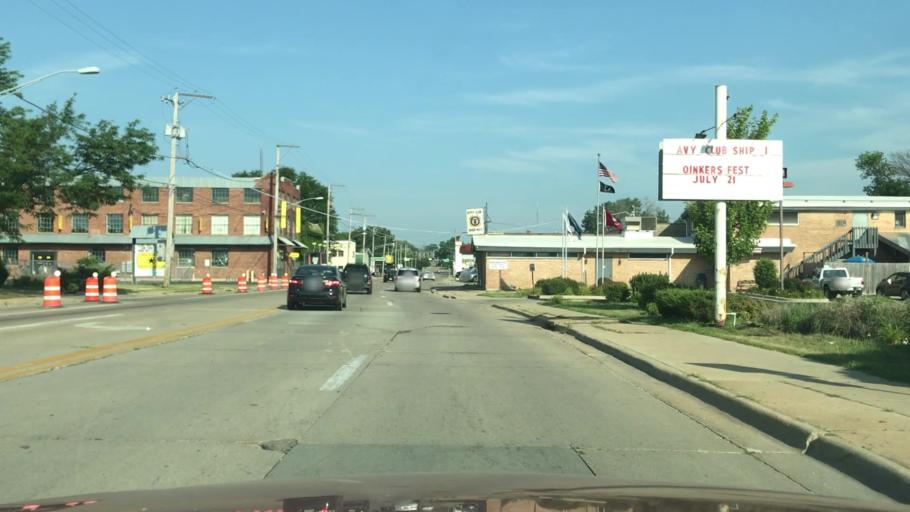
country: US
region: Illinois
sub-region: Winnebago County
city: Rockford
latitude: 42.2605
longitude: -89.0581
